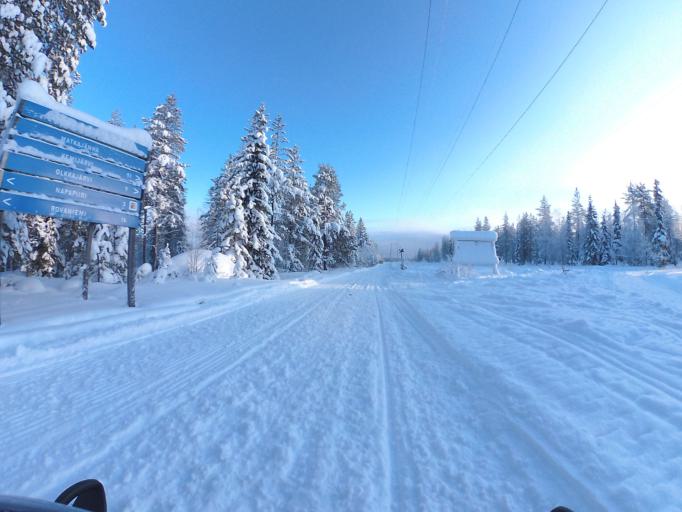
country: FI
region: Lapland
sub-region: Rovaniemi
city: Rovaniemi
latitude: 66.5284
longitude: 25.8851
